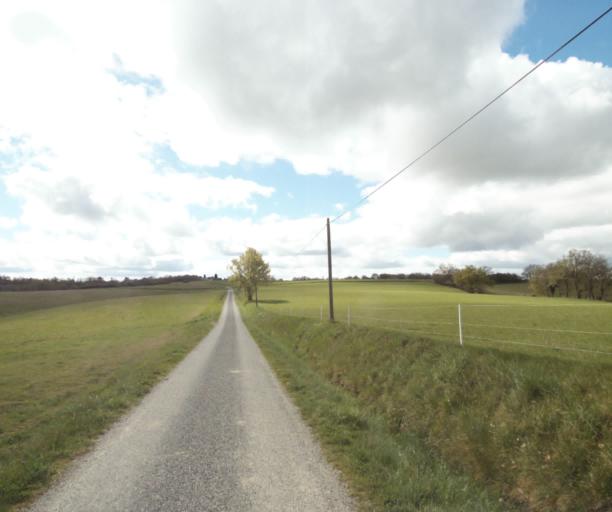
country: FR
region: Midi-Pyrenees
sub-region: Departement de l'Ariege
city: Saverdun
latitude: 43.1860
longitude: 1.5781
